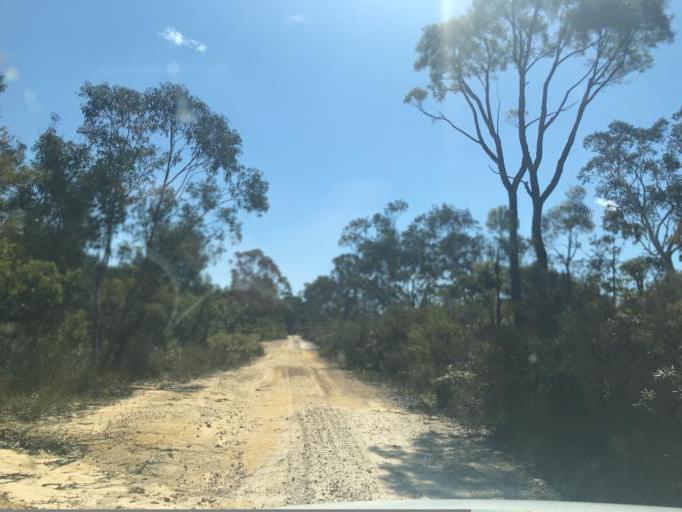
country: AU
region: New South Wales
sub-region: Wyong Shire
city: Little Jilliby
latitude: -33.1571
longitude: 151.0991
